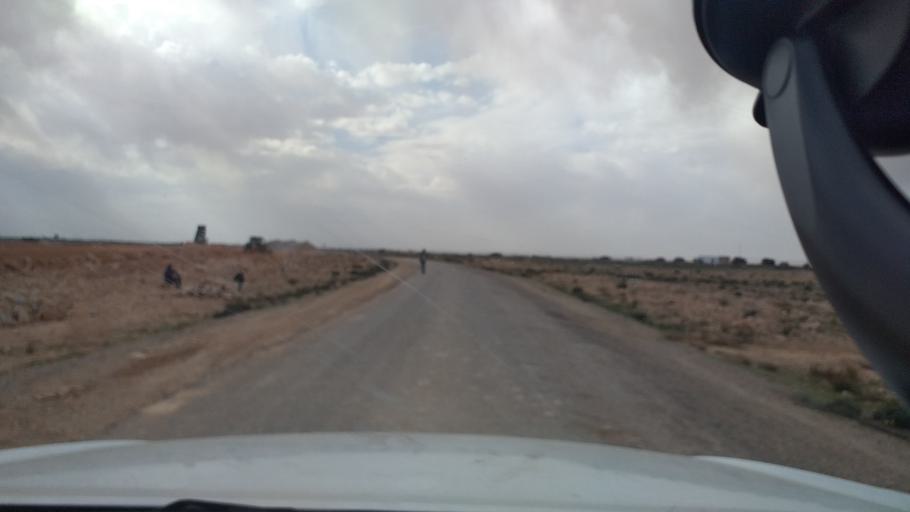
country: TN
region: Madanin
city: Medenine
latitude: 33.3051
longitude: 10.6121
